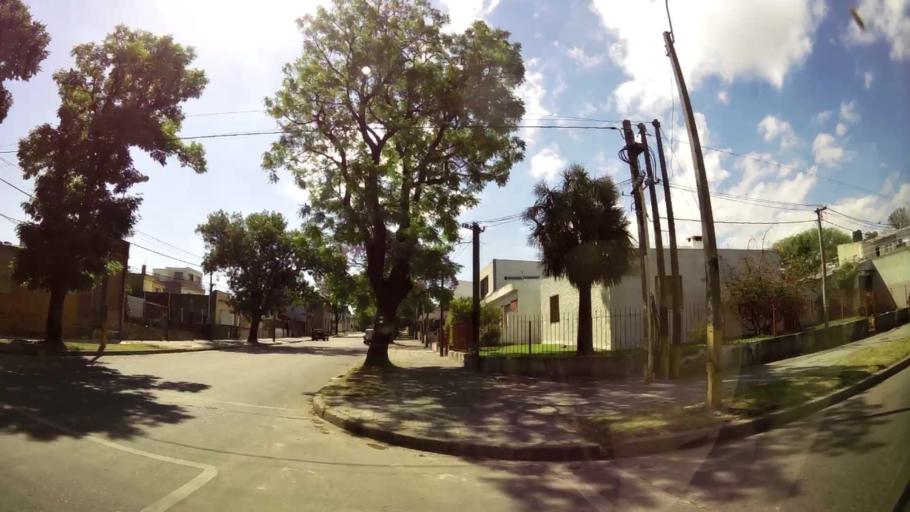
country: UY
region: Montevideo
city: Montevideo
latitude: -34.8624
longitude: -56.2218
